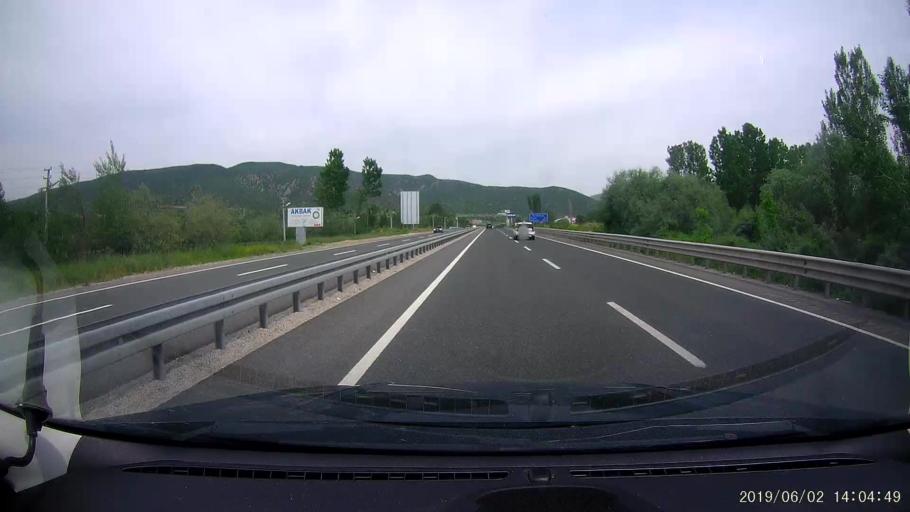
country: TR
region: Cankiri
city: Ilgaz
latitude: 40.9040
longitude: 33.6571
